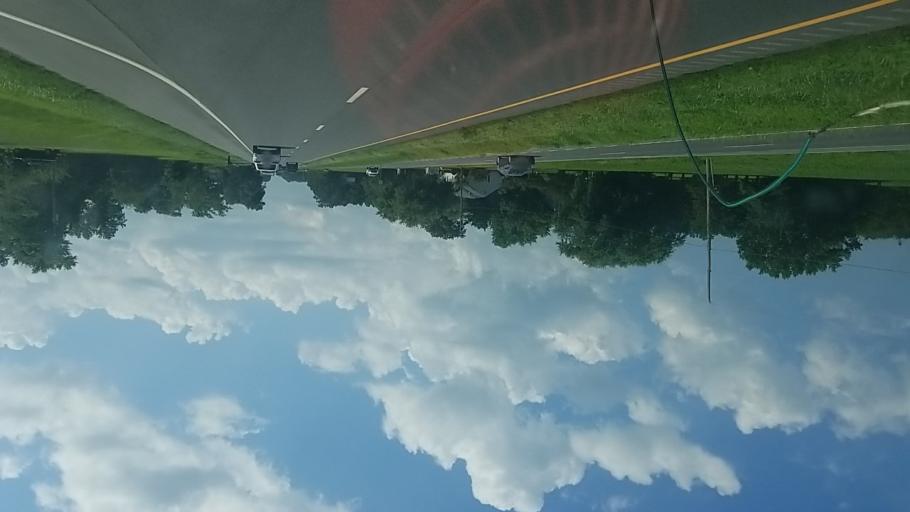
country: US
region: Delaware
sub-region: Sussex County
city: Selbyville
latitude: 38.5009
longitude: -75.2374
